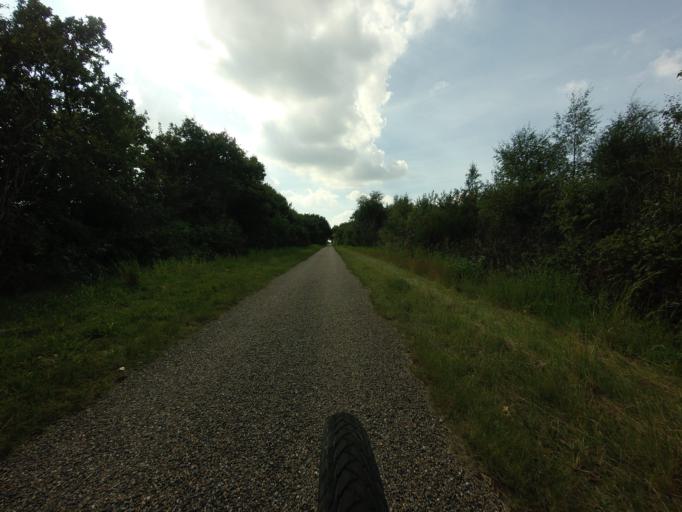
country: DK
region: Central Jutland
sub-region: Herning Kommune
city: Sunds
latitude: 56.2261
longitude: 9.0709
